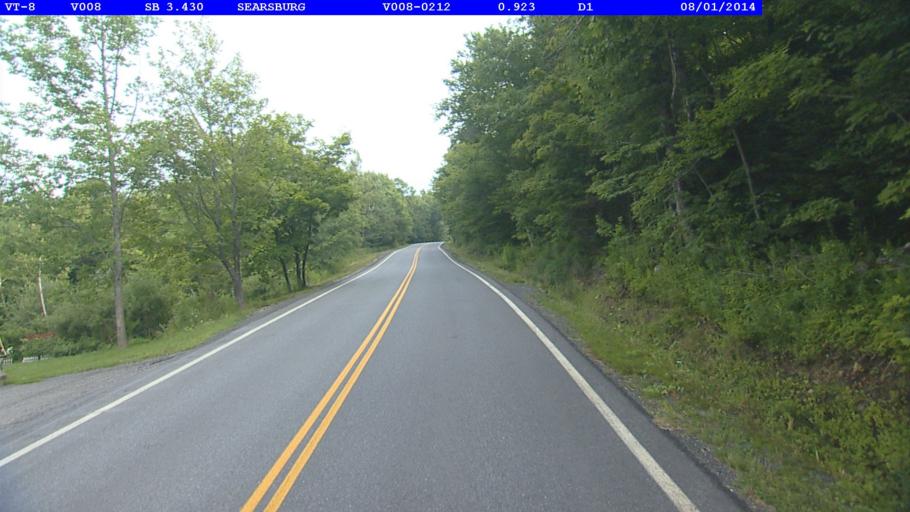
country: US
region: Vermont
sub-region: Windham County
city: Dover
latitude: 42.8707
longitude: -72.9709
